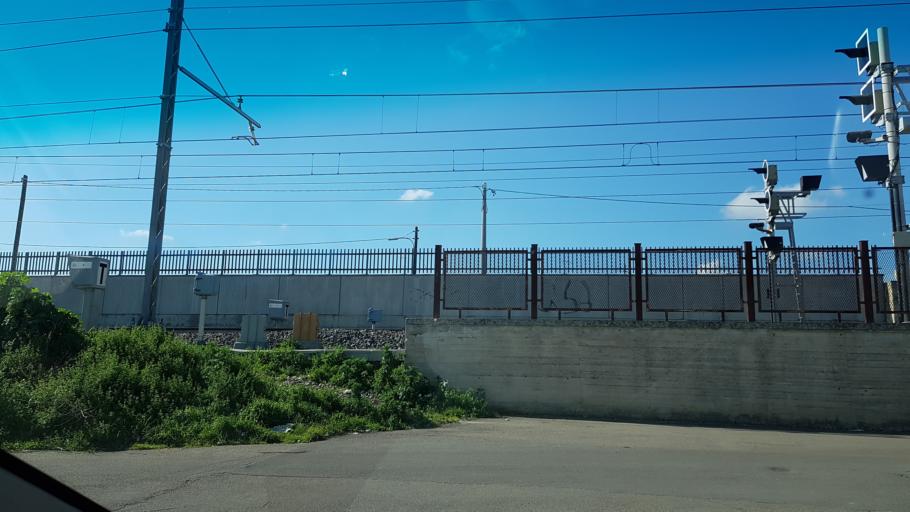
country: IT
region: Apulia
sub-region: Provincia di Lecce
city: Squinzano
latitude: 40.4324
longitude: 18.0537
